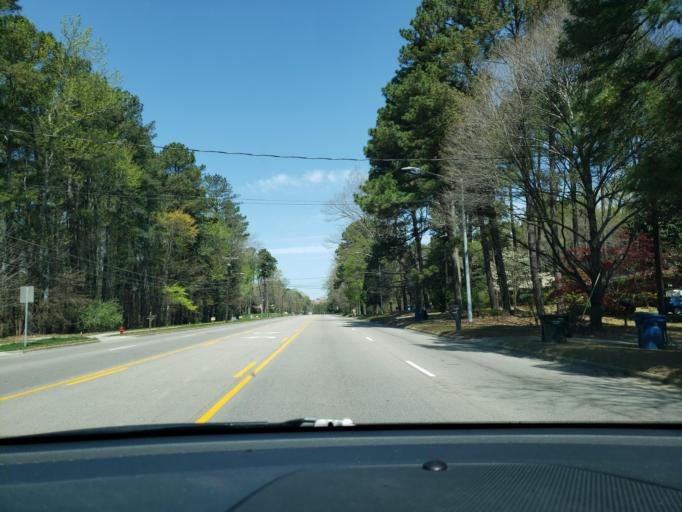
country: US
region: North Carolina
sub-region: Durham County
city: Durham
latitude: 35.9584
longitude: -78.8927
